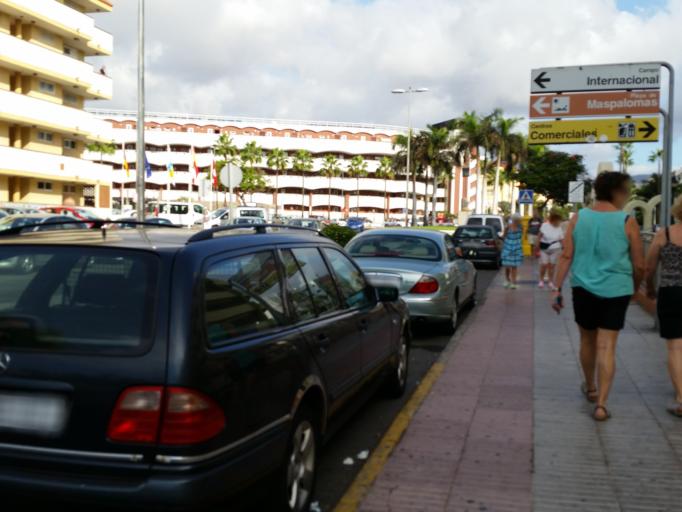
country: ES
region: Canary Islands
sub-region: Provincia de Las Palmas
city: Playa del Ingles
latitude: 27.7591
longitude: -15.5790
